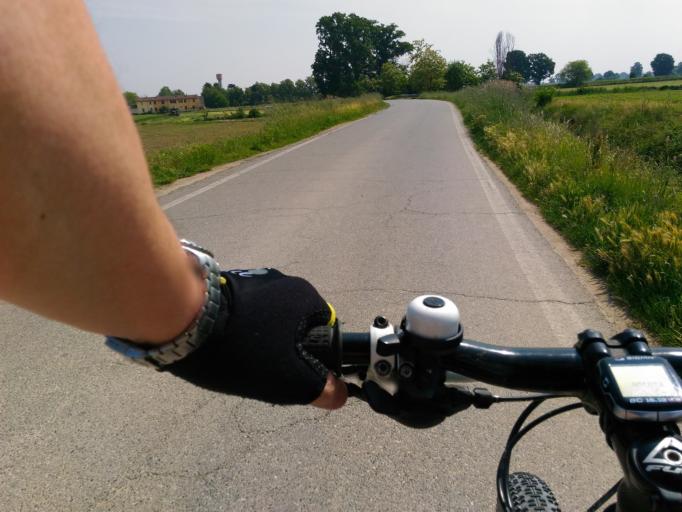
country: IT
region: Lombardy
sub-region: Provincia di Lodi
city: Bargano
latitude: 45.2416
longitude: 9.4548
